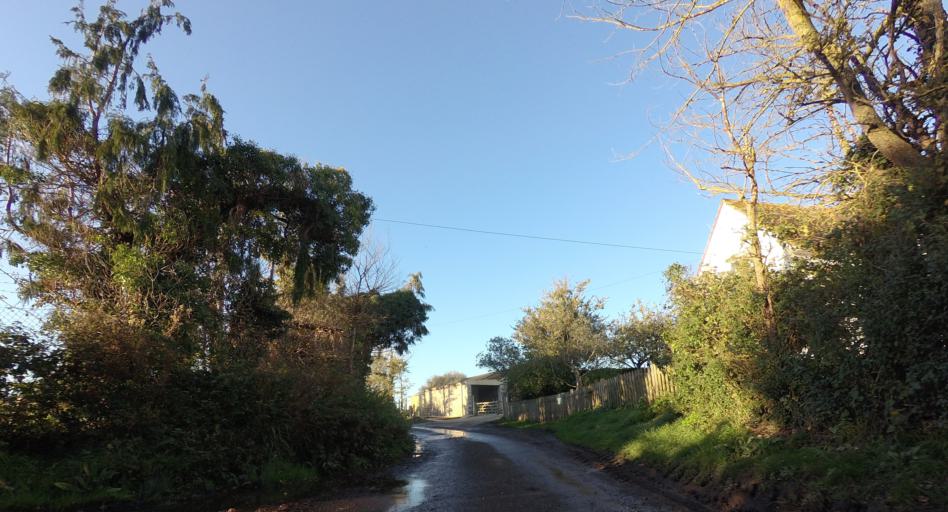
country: GB
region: England
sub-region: West Sussex
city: Steyning
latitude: 50.8958
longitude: -0.3144
